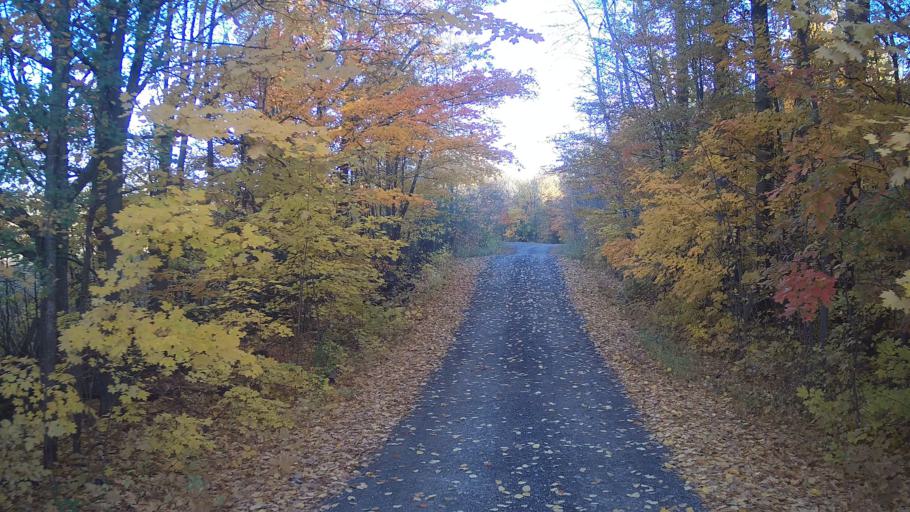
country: CA
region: Ontario
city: Arnprior
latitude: 45.3321
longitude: -76.3692
